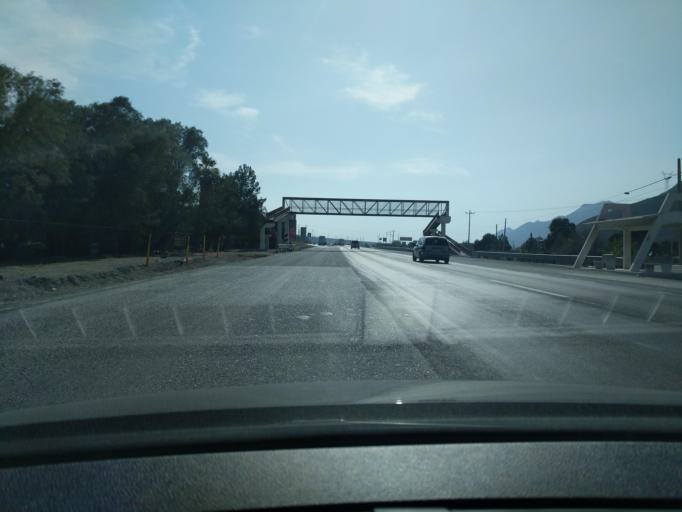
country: MX
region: Coahuila
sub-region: Ramos Arizpe
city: Ramos Arizpe
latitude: 25.6344
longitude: -100.7970
